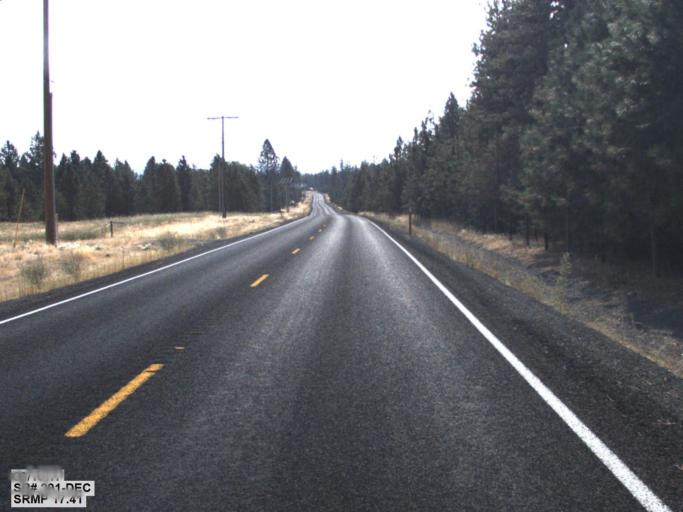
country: US
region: Washington
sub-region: Spokane County
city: Deer Park
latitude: 47.8486
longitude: -117.6340
